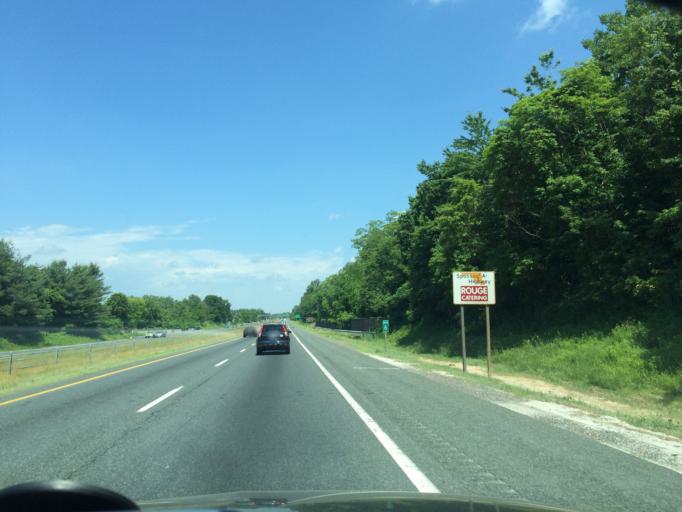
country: US
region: Maryland
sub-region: Baltimore County
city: Owings Mills
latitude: 39.4286
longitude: -76.8091
